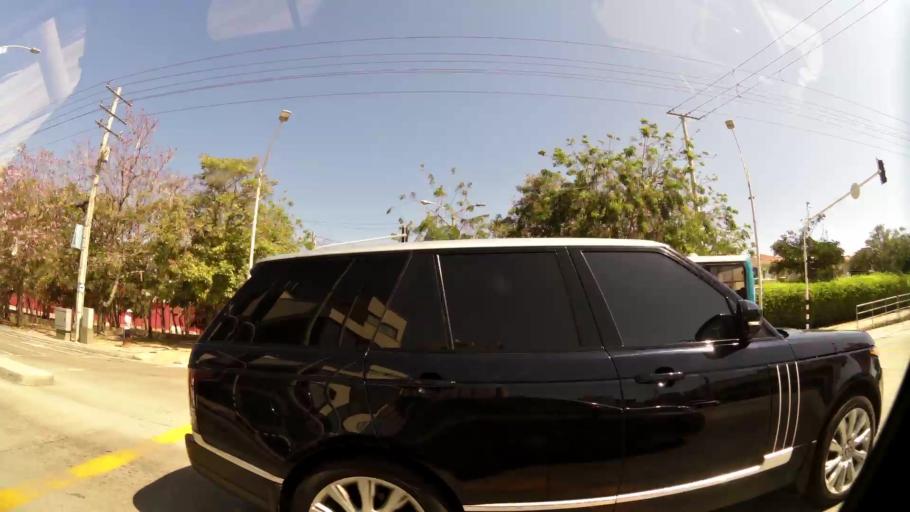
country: CO
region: Atlantico
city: Barranquilla
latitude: 11.0143
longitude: -74.8360
